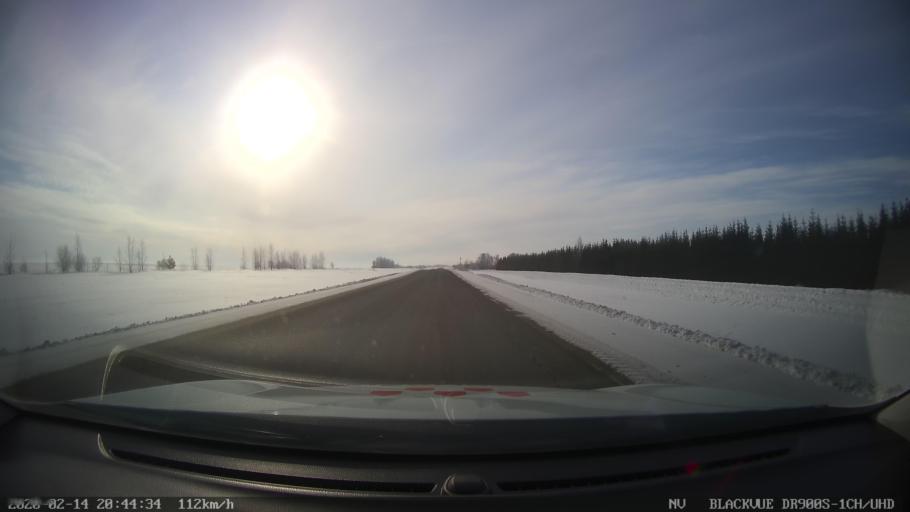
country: RU
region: Tatarstan
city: Kuybyshevskiy Zaton
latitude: 55.2917
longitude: 49.1456
